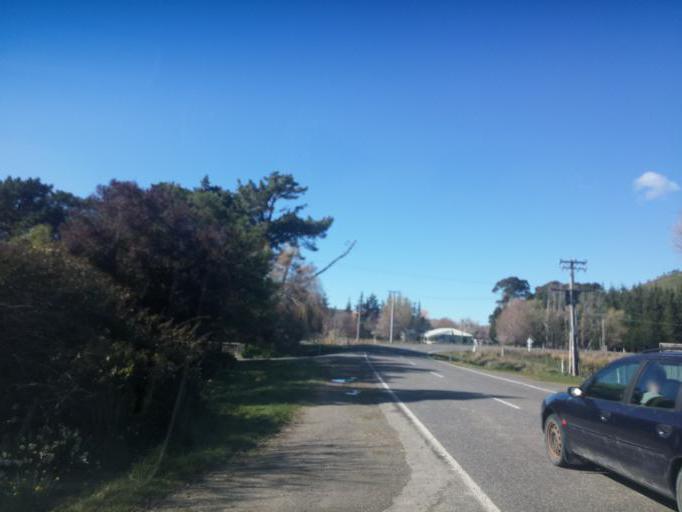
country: NZ
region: Wellington
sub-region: South Wairarapa District
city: Waipawa
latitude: -41.4143
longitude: 175.4875
